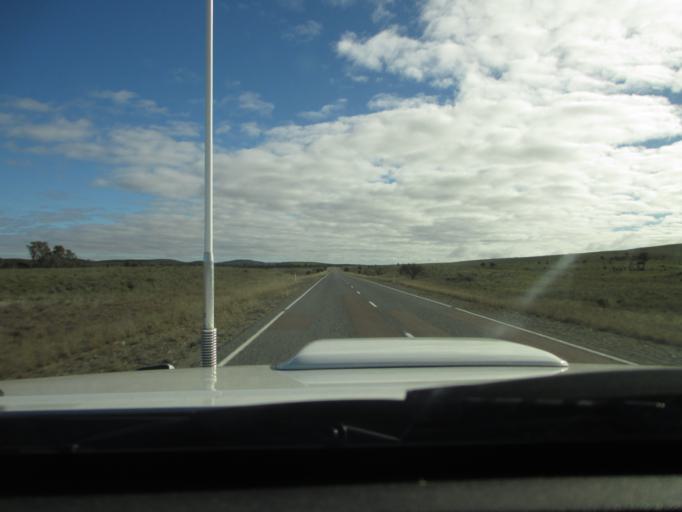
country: AU
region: South Australia
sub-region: Peterborough
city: Peterborough
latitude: -32.5970
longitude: 138.5642
